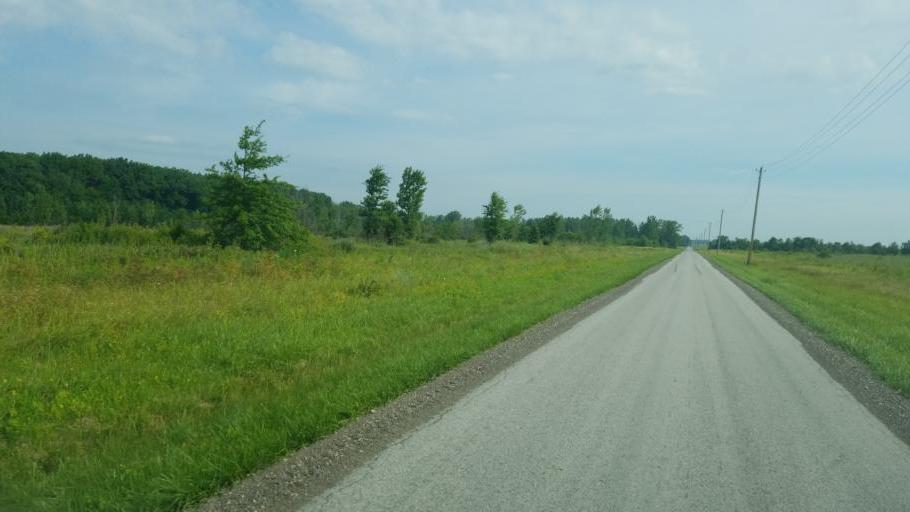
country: US
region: Ohio
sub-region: Marion County
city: Marion
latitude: 40.5698
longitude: -83.2558
